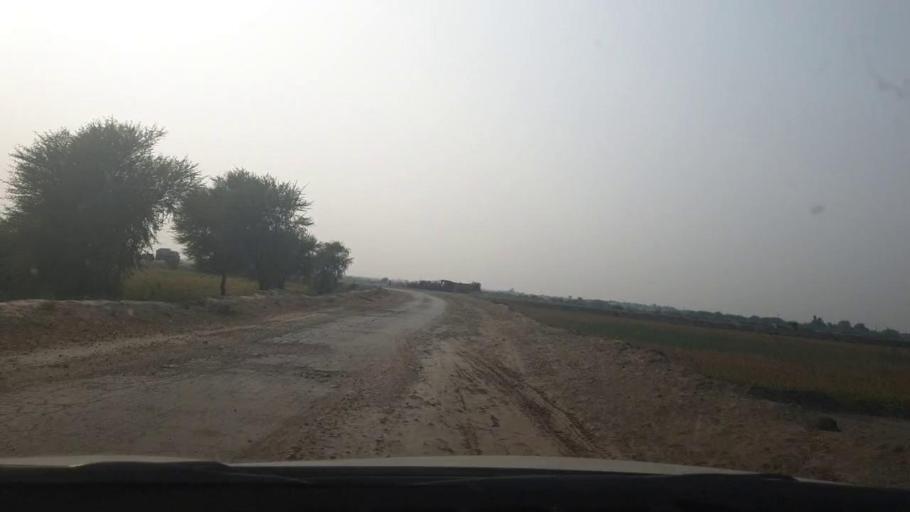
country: PK
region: Sindh
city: Bulri
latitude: 24.7856
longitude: 68.4206
